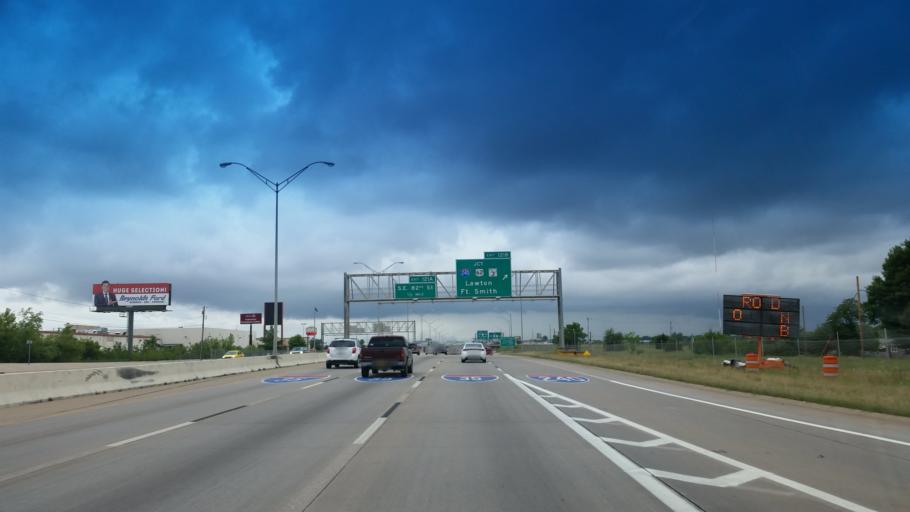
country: US
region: Oklahoma
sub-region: Cleveland County
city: Moore
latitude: 35.3970
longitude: -97.4952
